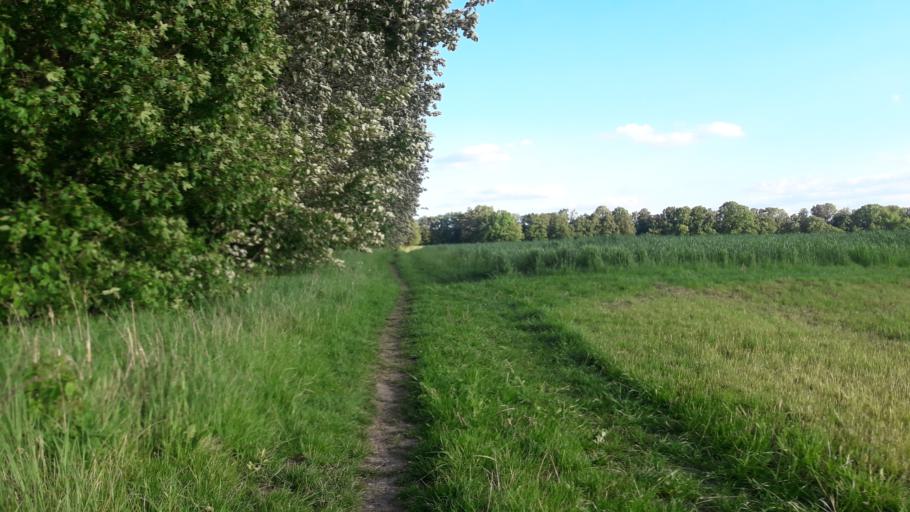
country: DE
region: North Rhine-Westphalia
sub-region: Regierungsbezirk Detmold
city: Paderborn
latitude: 51.6661
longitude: 8.7944
